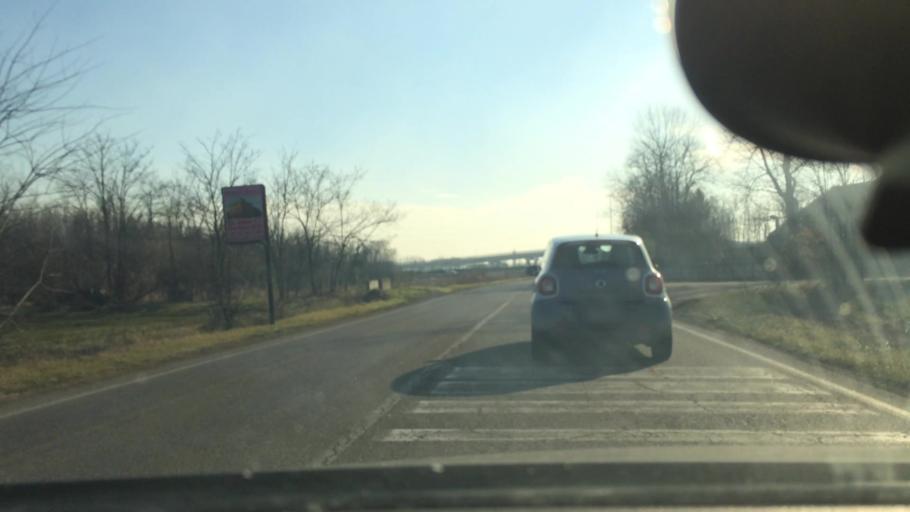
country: IT
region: Lombardy
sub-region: Citta metropolitana di Milano
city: Arluno
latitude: 45.5048
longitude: 8.9298
